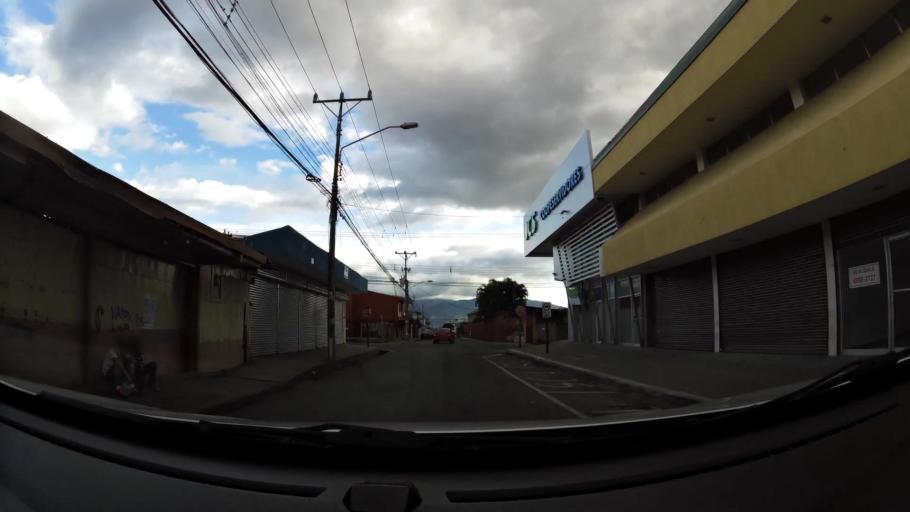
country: CR
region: Alajuela
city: Alajuela
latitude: 10.0139
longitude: -84.2163
